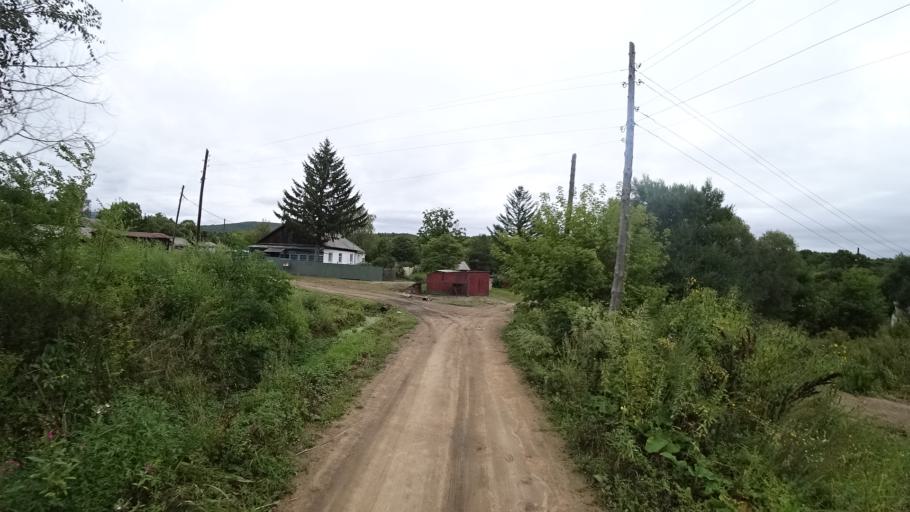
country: RU
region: Primorskiy
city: Rettikhovka
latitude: 44.1721
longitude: 132.7704
